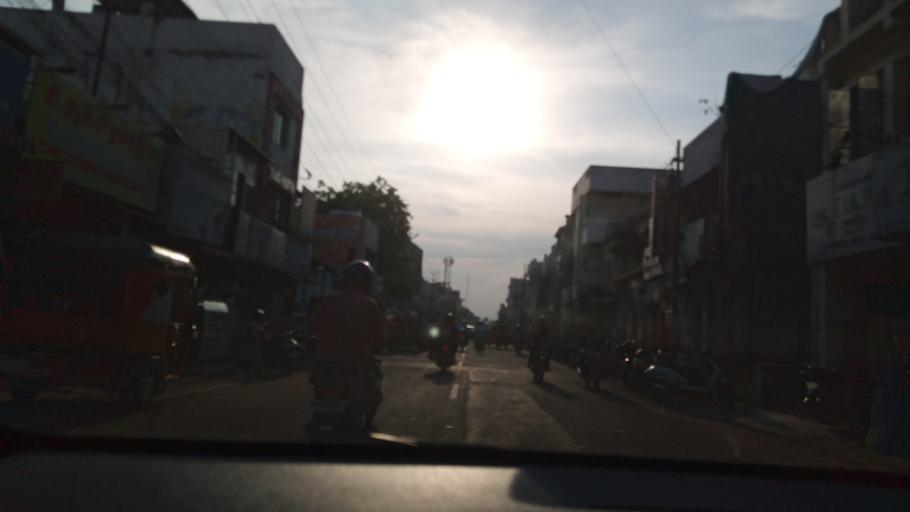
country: IN
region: Tamil Nadu
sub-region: Coimbatore
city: Coimbatore
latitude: 10.9923
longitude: 76.9583
